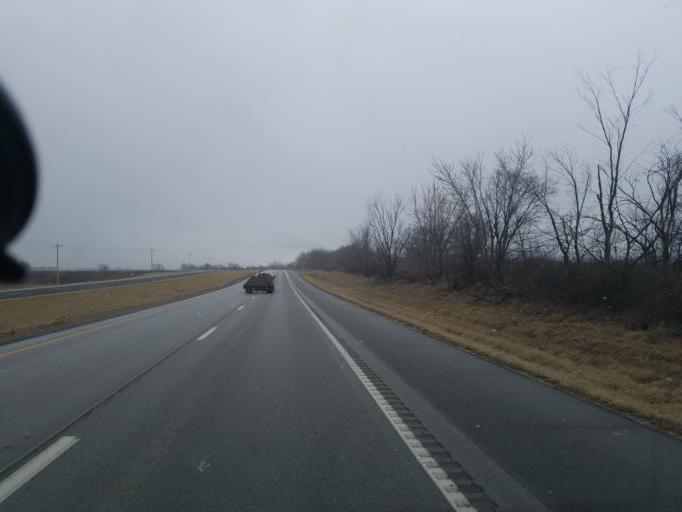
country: US
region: Missouri
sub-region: Macon County
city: Macon
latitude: 39.8733
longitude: -92.4774
